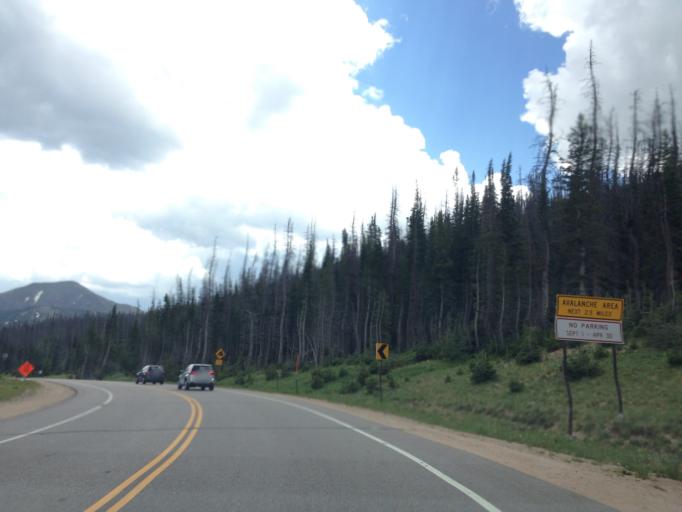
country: US
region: Colorado
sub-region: Larimer County
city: Estes Park
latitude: 40.5191
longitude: -105.8933
